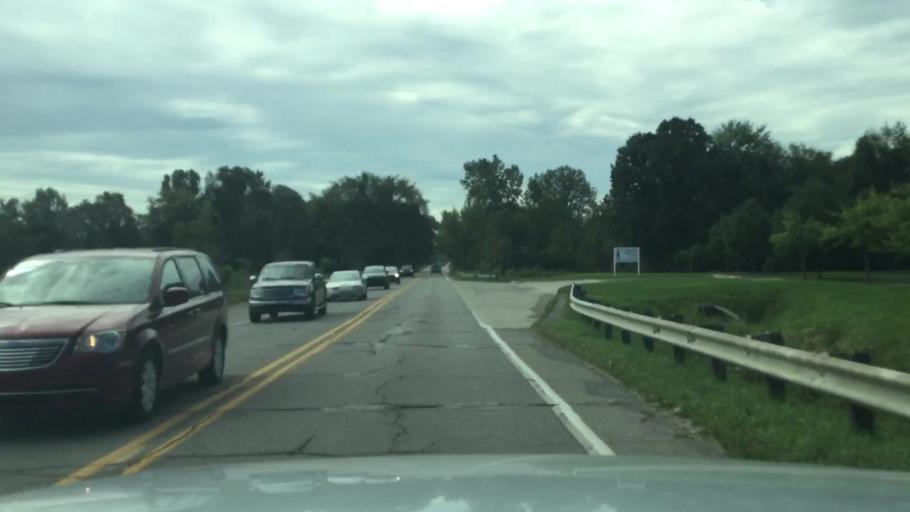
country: US
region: Michigan
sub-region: Wayne County
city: Belleville
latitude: 42.1807
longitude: -83.4831
